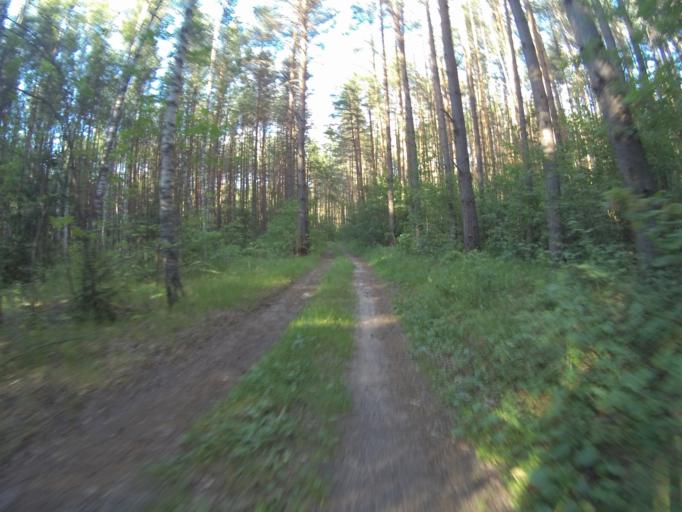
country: RU
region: Vladimir
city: Bogolyubovo
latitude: 56.1404
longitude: 40.5436
